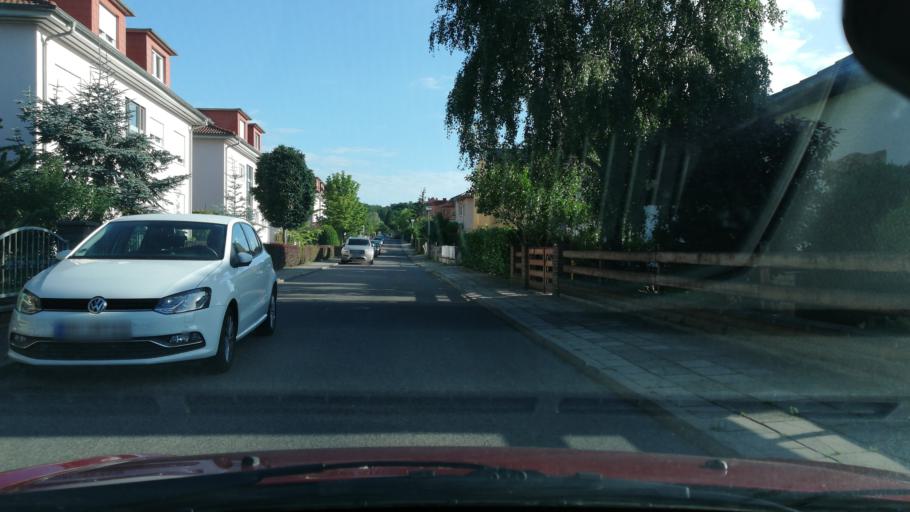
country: DE
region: Saxony-Anhalt
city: Halle Neustadt
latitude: 51.4915
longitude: 11.9091
